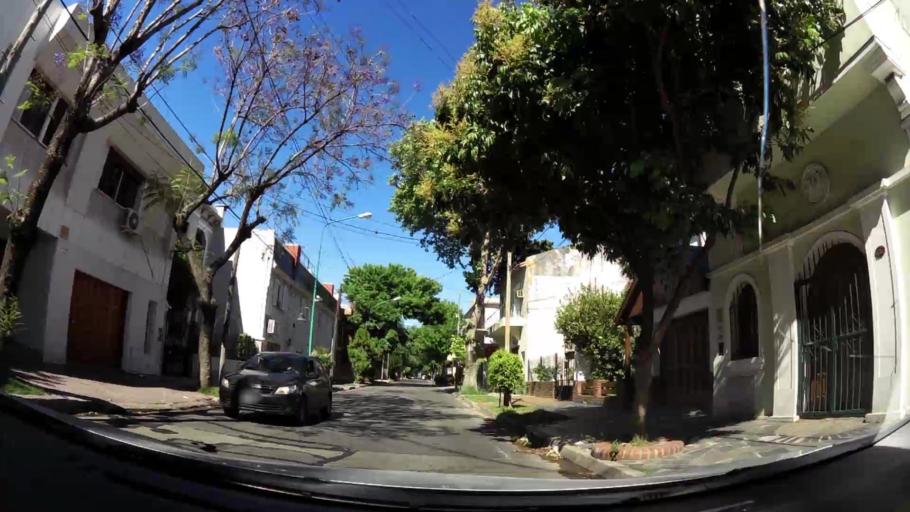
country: AR
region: Buenos Aires
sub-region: Partido de Vicente Lopez
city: Olivos
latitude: -34.5337
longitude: -58.4735
